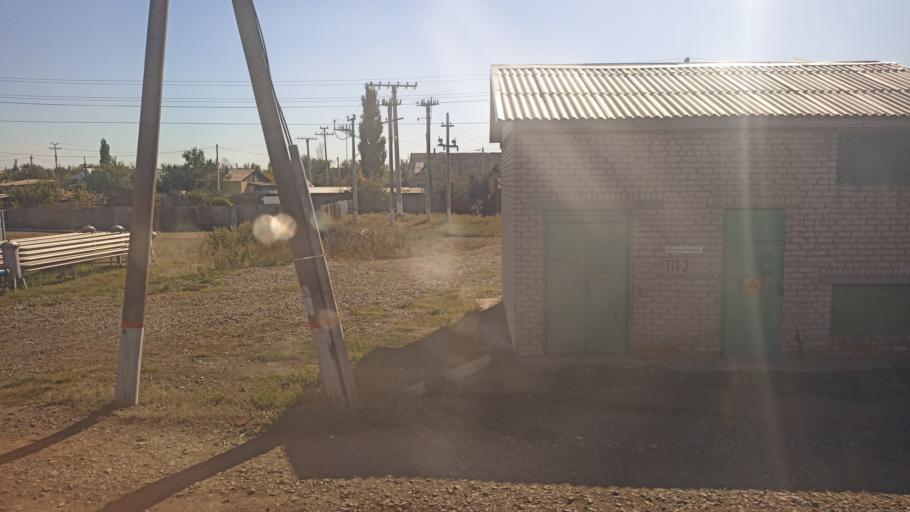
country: RU
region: Saratov
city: Pushkino
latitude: 51.2353
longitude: 46.9811
